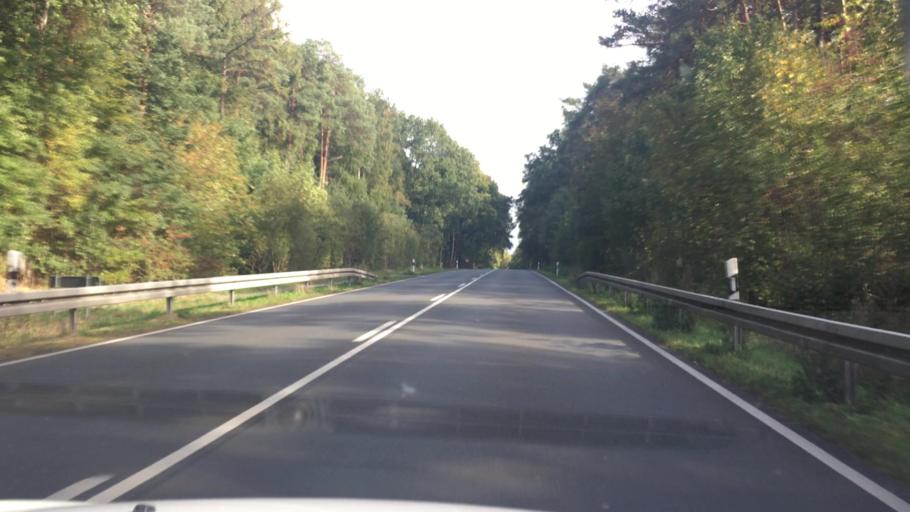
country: DE
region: Lower Saxony
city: Hemsloh
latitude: 52.6113
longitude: 8.5281
